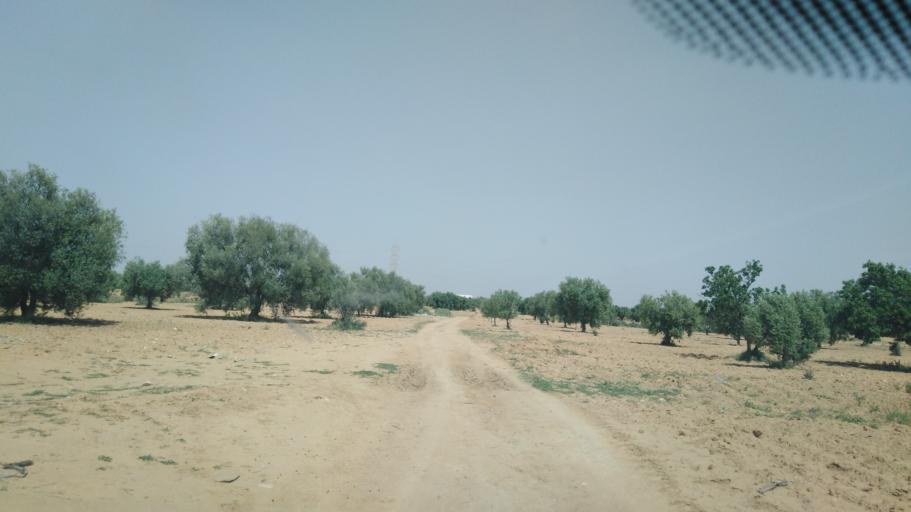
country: TN
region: Safaqis
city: Sfax
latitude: 34.7372
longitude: 10.5734
